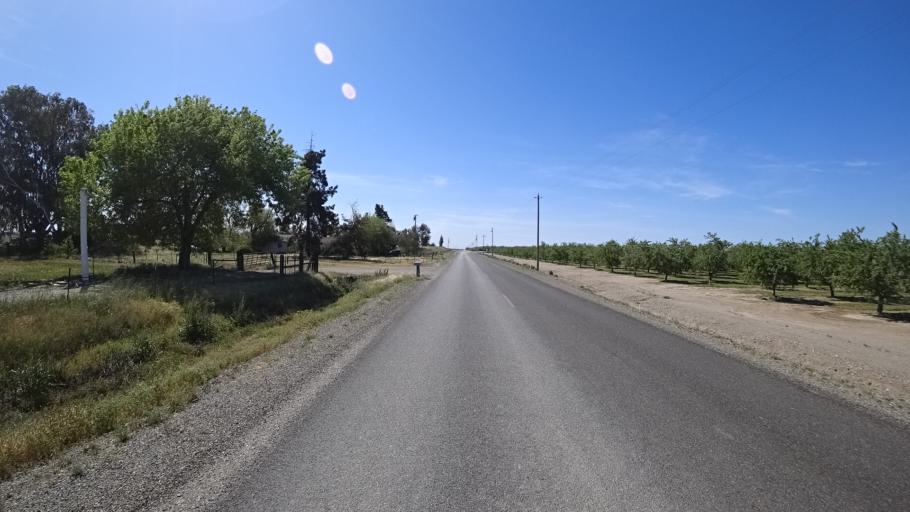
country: US
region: California
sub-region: Glenn County
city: Hamilton City
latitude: 39.6894
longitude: -122.1032
